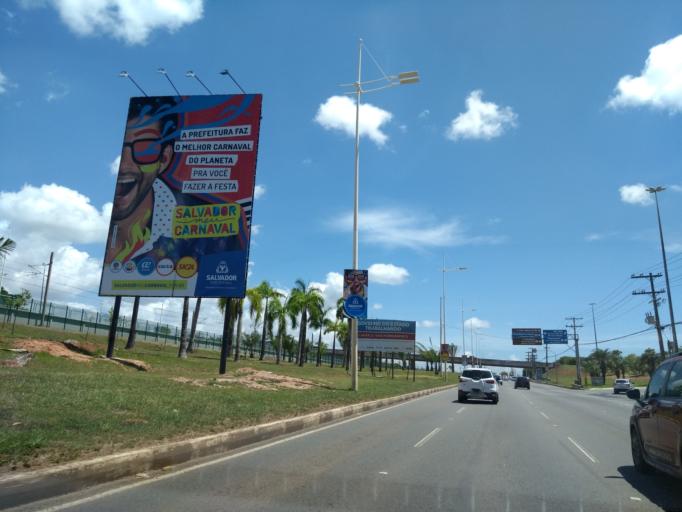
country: BR
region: Bahia
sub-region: Salvador
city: Salvador
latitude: -12.9518
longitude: -38.4257
